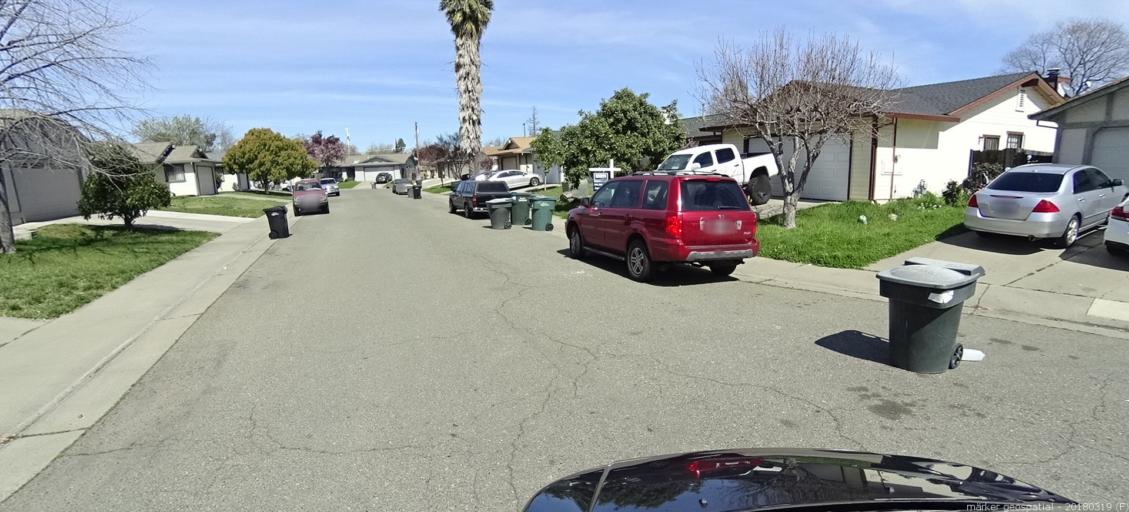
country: US
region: California
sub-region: Sacramento County
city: Parkway
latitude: 38.5166
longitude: -121.4428
